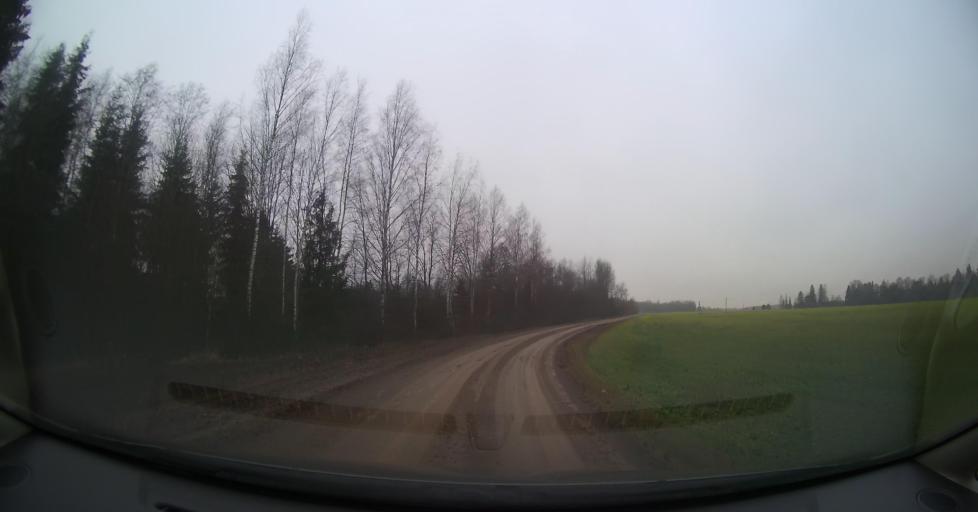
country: EE
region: Tartu
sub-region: Tartu linn
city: Tartu
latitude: 58.3933
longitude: 26.9272
